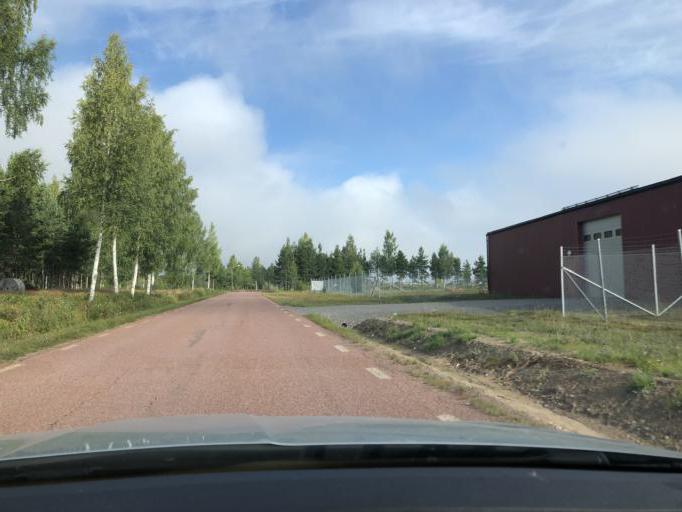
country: SE
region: Dalarna
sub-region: Mora Kommun
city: Mora
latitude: 60.9592
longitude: 14.5029
